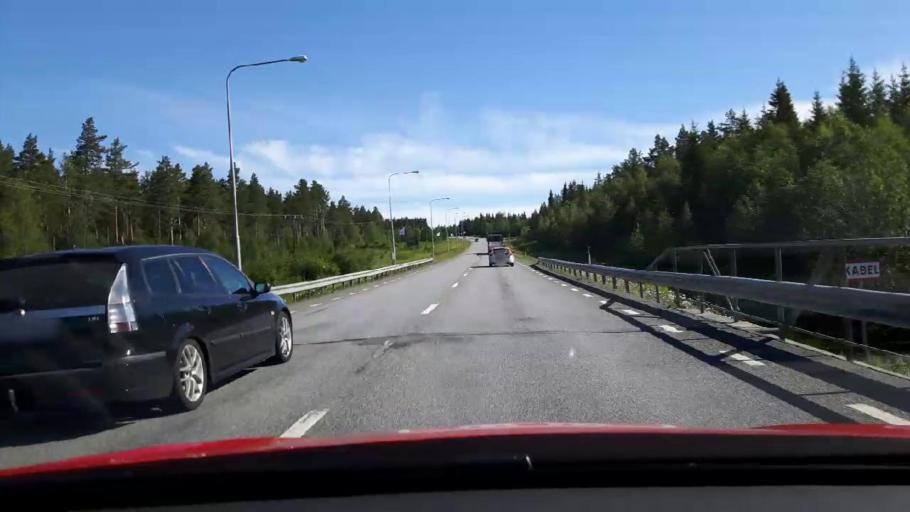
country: SE
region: Jaemtland
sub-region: OEstersunds Kommun
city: Lit
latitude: 63.3768
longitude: 14.8833
